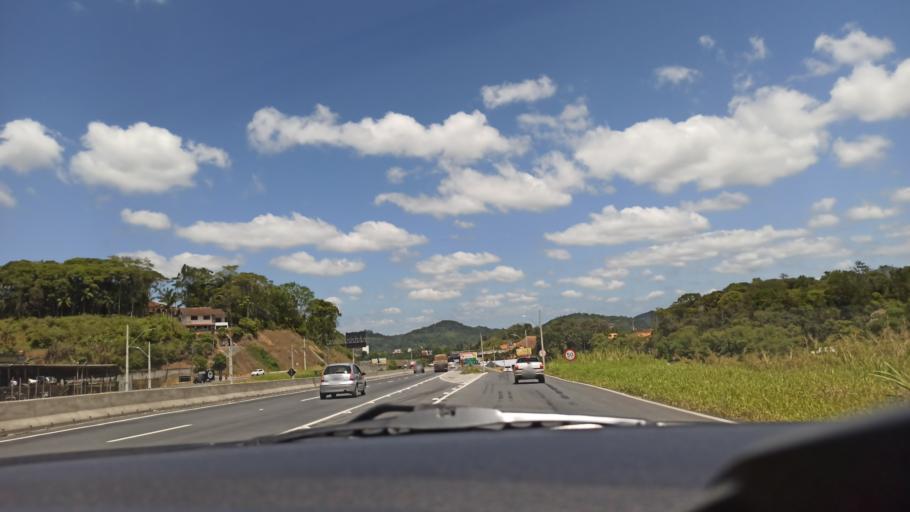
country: BR
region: Santa Catarina
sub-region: Blumenau
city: Blumenau
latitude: -26.8596
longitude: -49.0750
